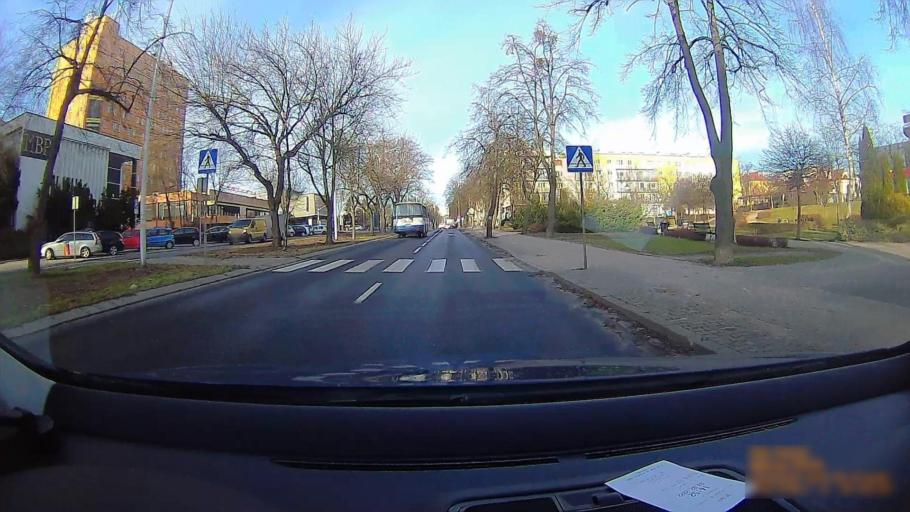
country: PL
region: Greater Poland Voivodeship
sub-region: Konin
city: Konin
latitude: 52.2276
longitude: 18.2507
